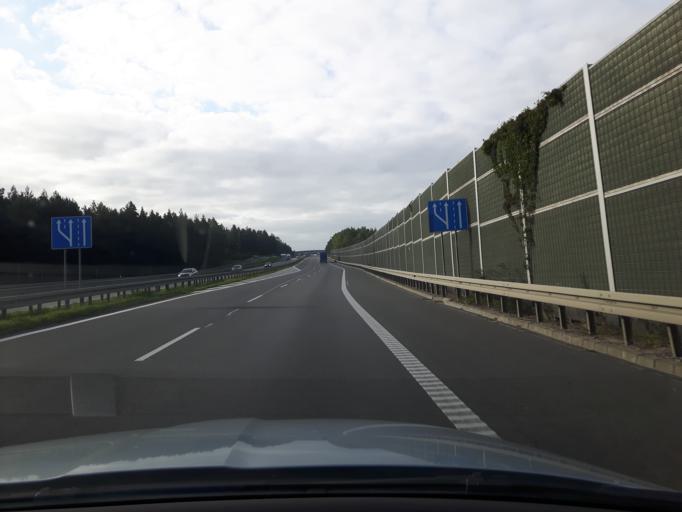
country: PL
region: Swietokrzyskie
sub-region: Powiat skarzyski
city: Suchedniow
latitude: 51.0870
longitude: 20.8359
